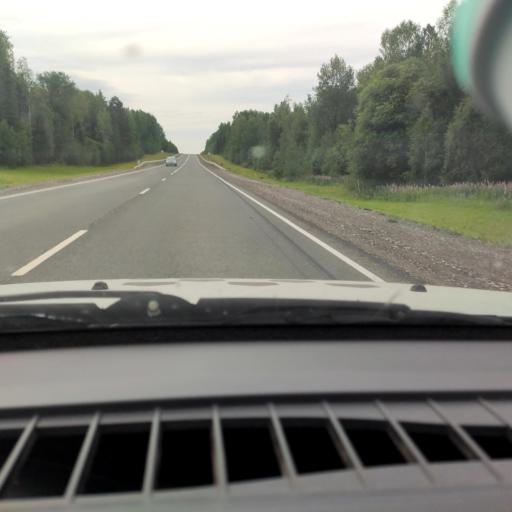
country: RU
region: Kirov
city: Kostino
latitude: 58.7930
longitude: 53.6001
